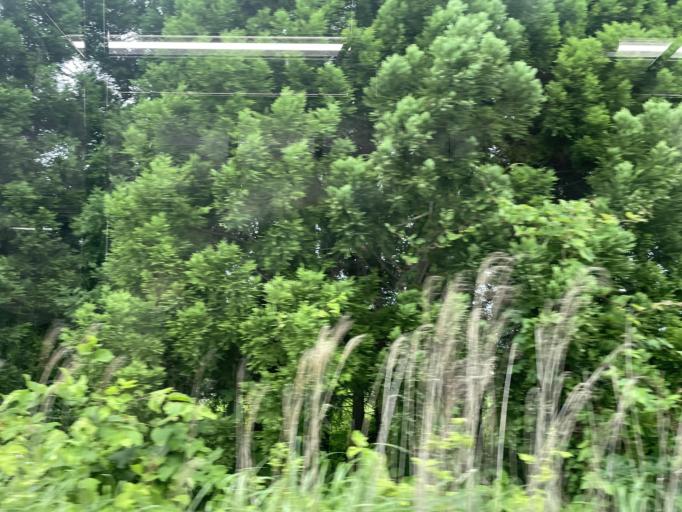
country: JP
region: Akita
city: Tenno
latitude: 39.9051
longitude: 139.8624
